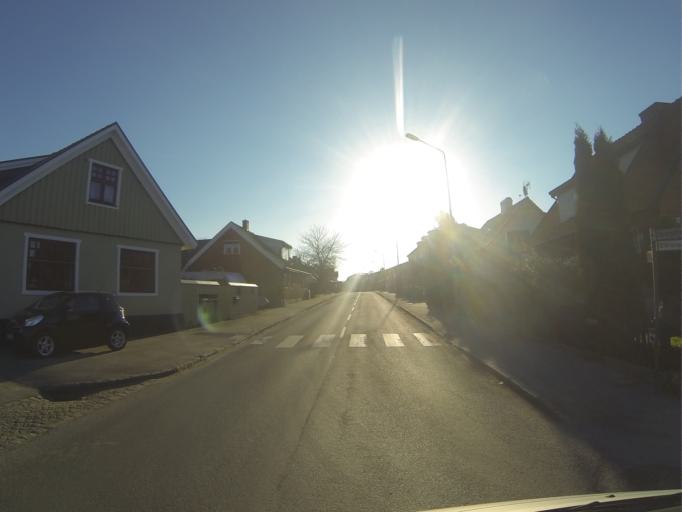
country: SE
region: Skane
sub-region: Hoors Kommun
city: Loberod
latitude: 55.7766
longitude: 13.5155
